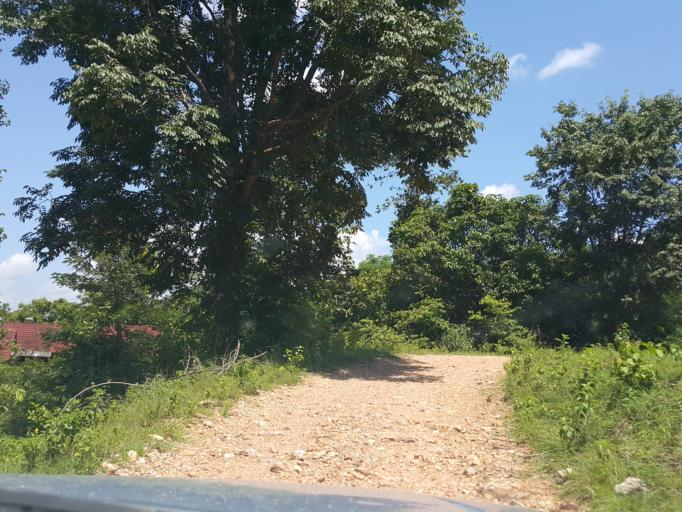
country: TH
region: Lamphun
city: Ban Thi
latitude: 18.6835
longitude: 99.1744
